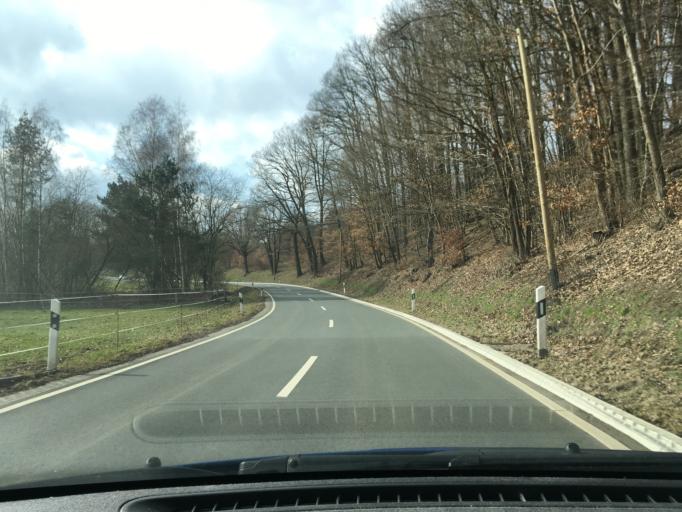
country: DE
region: Lower Saxony
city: Uslar
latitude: 51.5861
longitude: 9.6663
